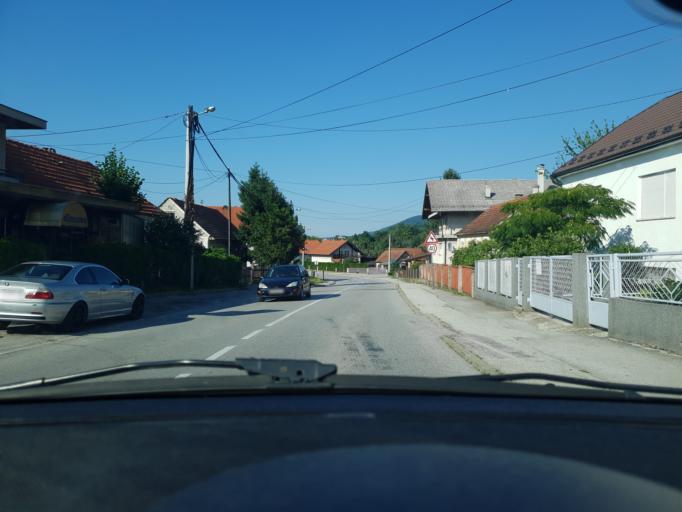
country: HR
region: Zagrebacka
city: Jablanovec
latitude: 45.8799
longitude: 15.8544
